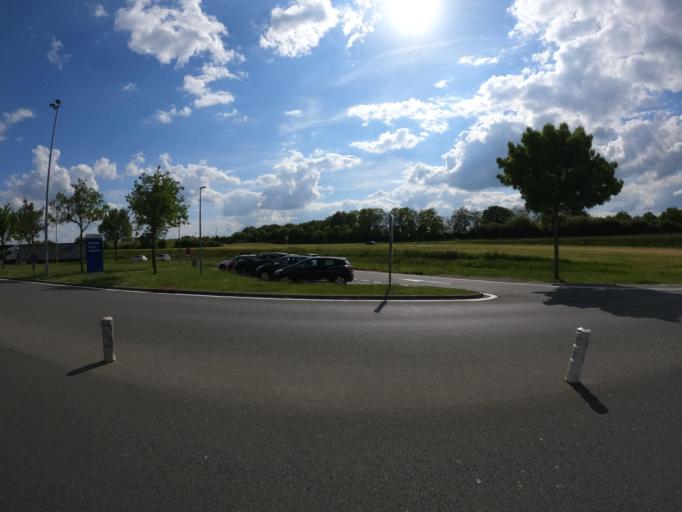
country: FR
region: Pays de la Loire
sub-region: Departement de Maine-et-Loire
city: La Tessoualle
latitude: 47.0200
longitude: -0.8817
